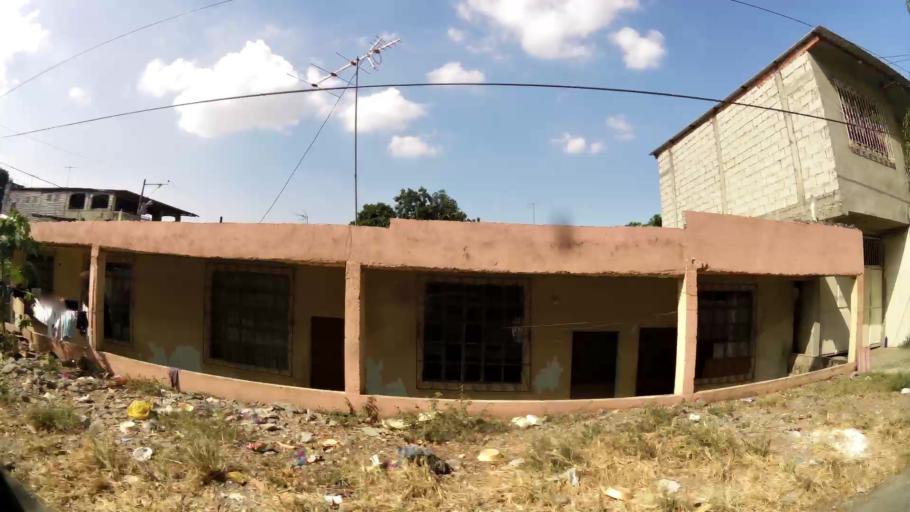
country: EC
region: Guayas
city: Guayaquil
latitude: -2.1615
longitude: -79.9376
